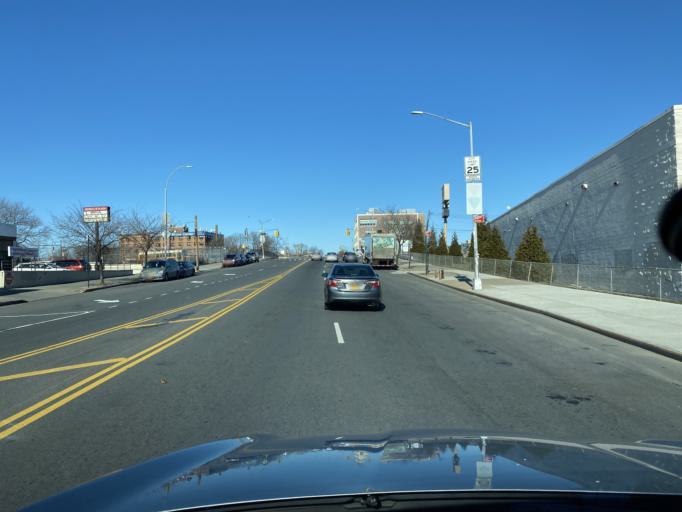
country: US
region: New York
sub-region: Bronx
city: The Bronx
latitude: 40.8248
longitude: -73.8590
